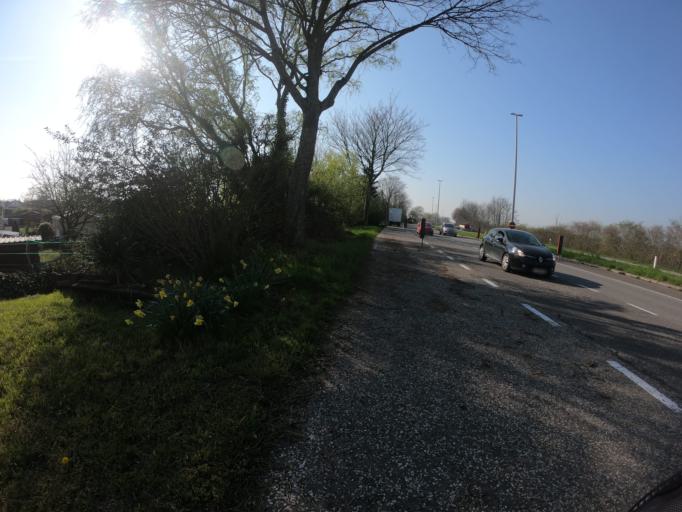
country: BE
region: Flanders
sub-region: Provincie Limburg
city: Sint-Truiden
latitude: 50.8173
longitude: 5.2424
